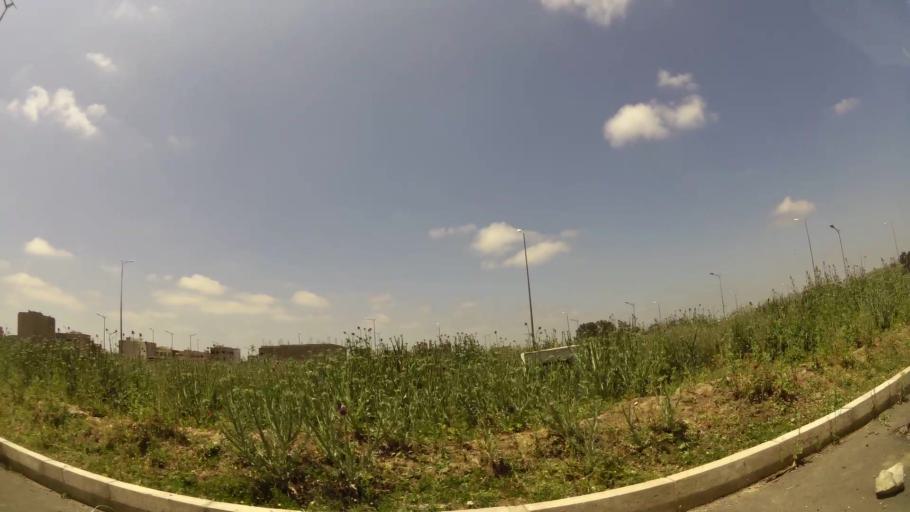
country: MA
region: Fes-Boulemane
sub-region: Fes
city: Fes
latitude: 34.0386
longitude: -5.0542
